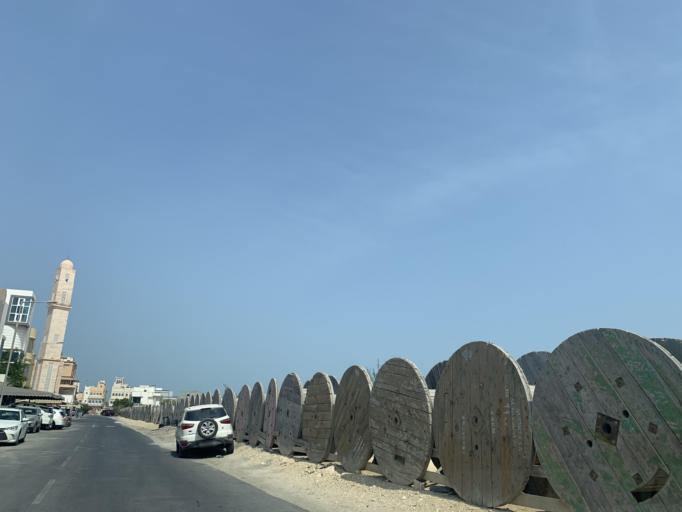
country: BH
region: Muharraq
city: Al Hadd
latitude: 26.2633
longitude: 50.6576
